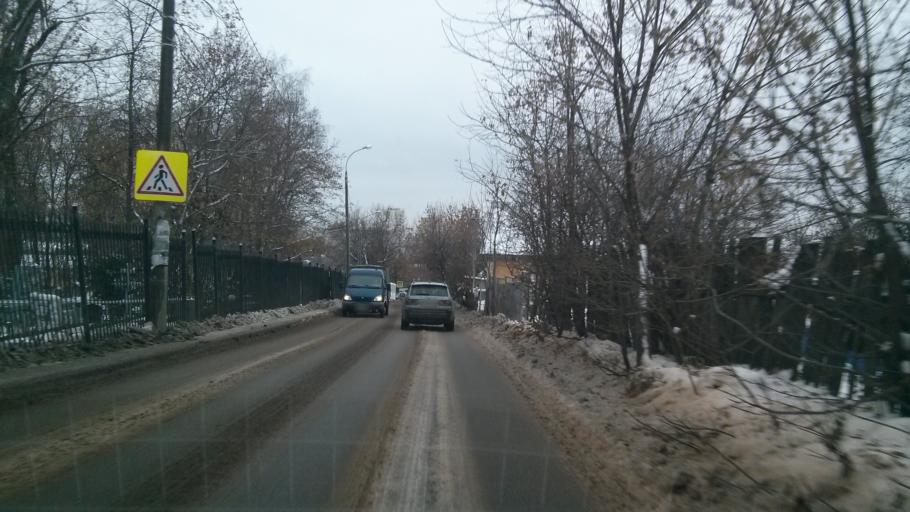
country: RU
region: Nizjnij Novgorod
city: Nizhniy Novgorod
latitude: 56.3085
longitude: 44.0491
